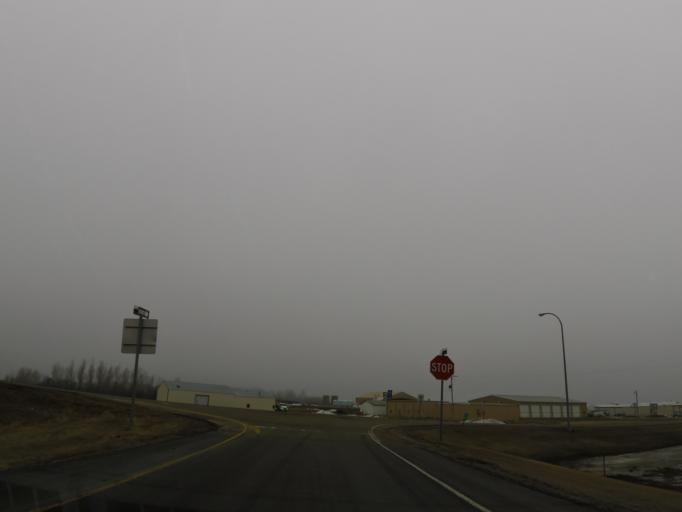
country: US
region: North Dakota
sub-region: Walsh County
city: Grafton
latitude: 48.5710
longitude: -97.1850
